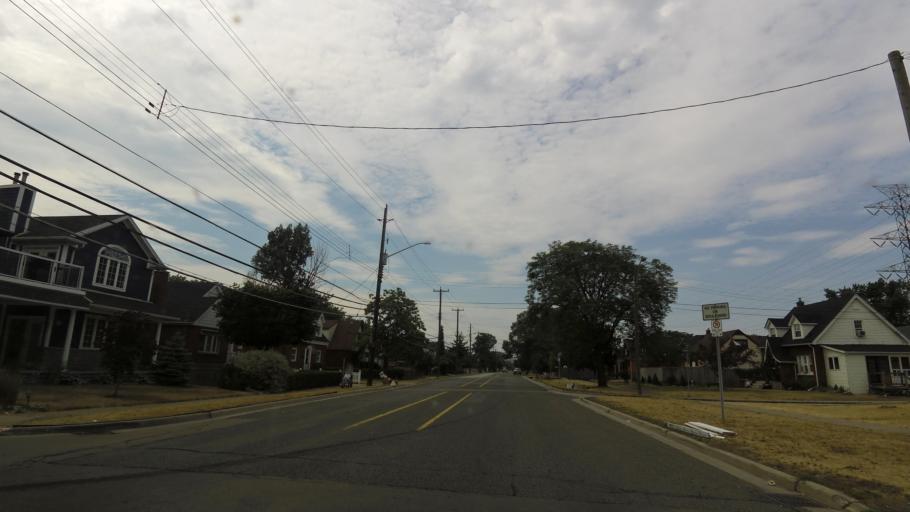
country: CA
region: Ontario
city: Hamilton
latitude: 43.2784
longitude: -79.7832
